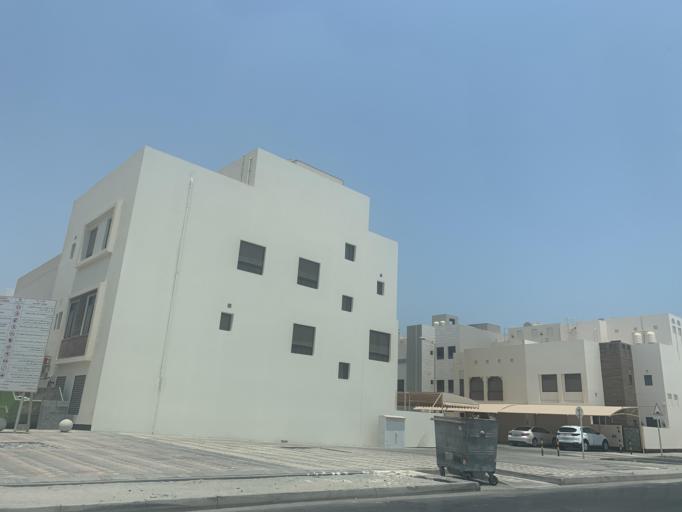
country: BH
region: Muharraq
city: Al Hadd
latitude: 26.2346
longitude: 50.6765
